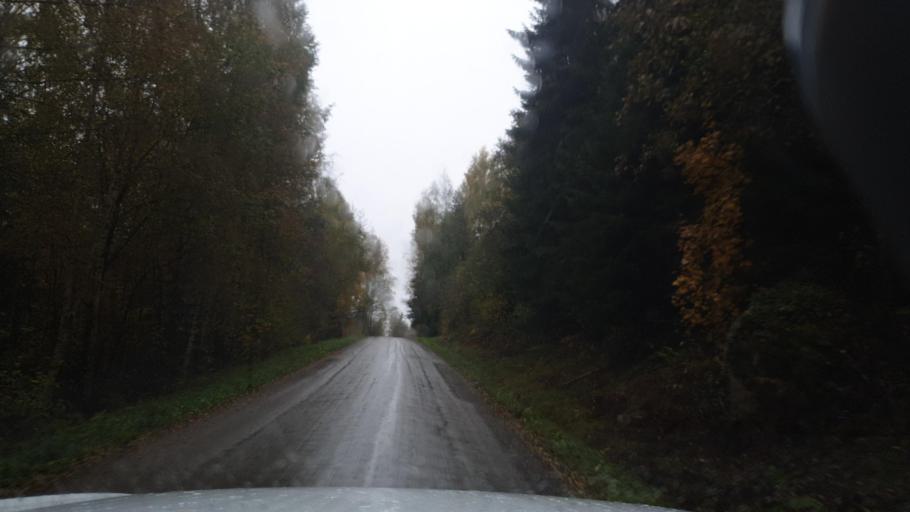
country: SE
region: Vaermland
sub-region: Eda Kommun
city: Amotfors
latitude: 59.7378
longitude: 12.2780
